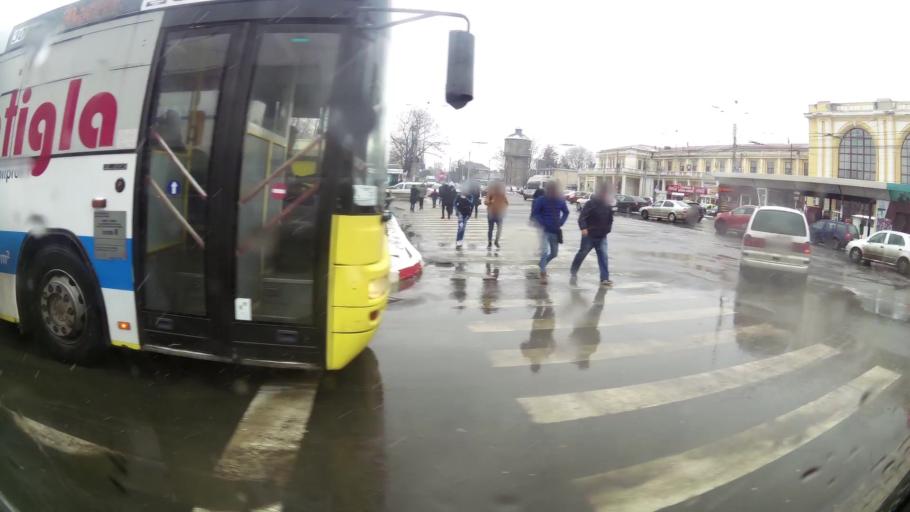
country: RO
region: Prahova
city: Ploiesti
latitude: 44.9258
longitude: 26.0293
